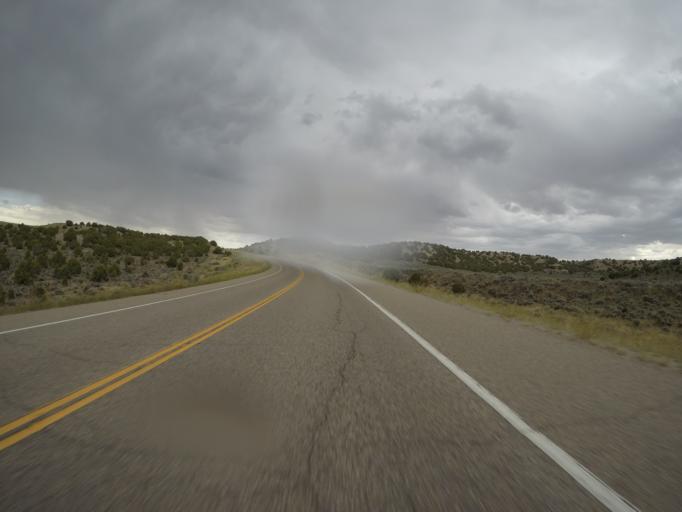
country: US
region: Colorado
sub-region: Rio Blanco County
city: Meeker
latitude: 40.4092
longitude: -108.3362
